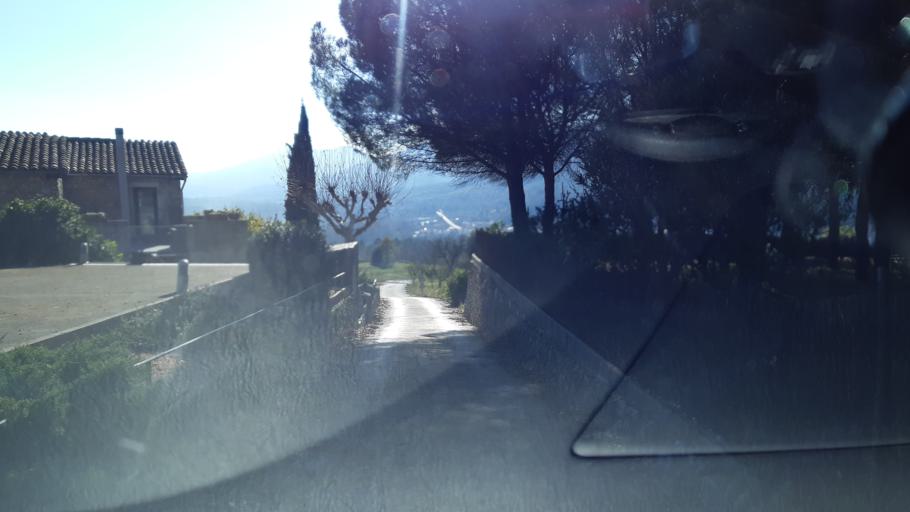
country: ES
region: Catalonia
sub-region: Provincia de Girona
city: la Cellera de Ter
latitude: 42.0172
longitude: 2.6077
